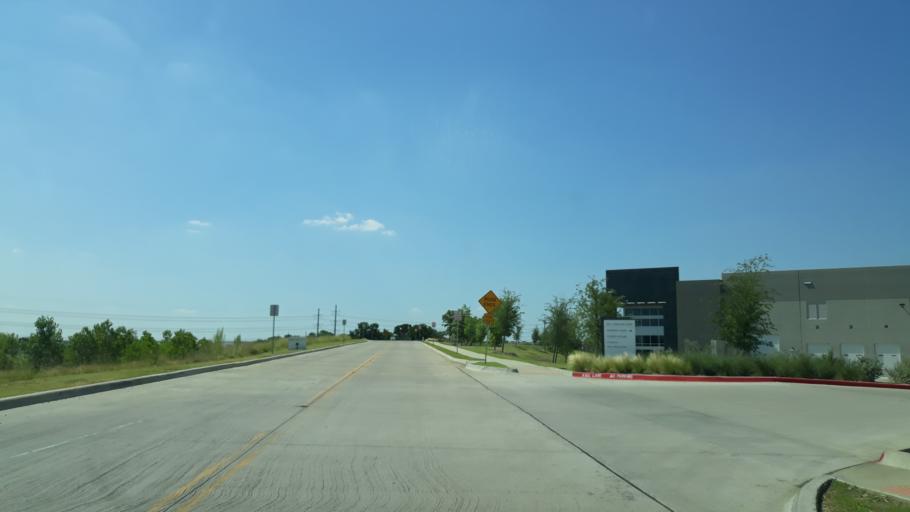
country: US
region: Texas
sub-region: Tarrant County
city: Euless
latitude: 32.8252
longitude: -97.0202
